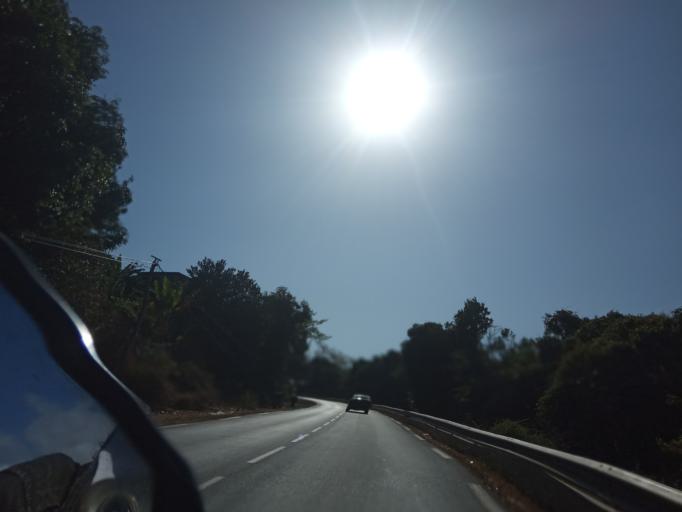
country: YT
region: Bandrele
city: Bandrele
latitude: -12.9162
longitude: 45.1892
